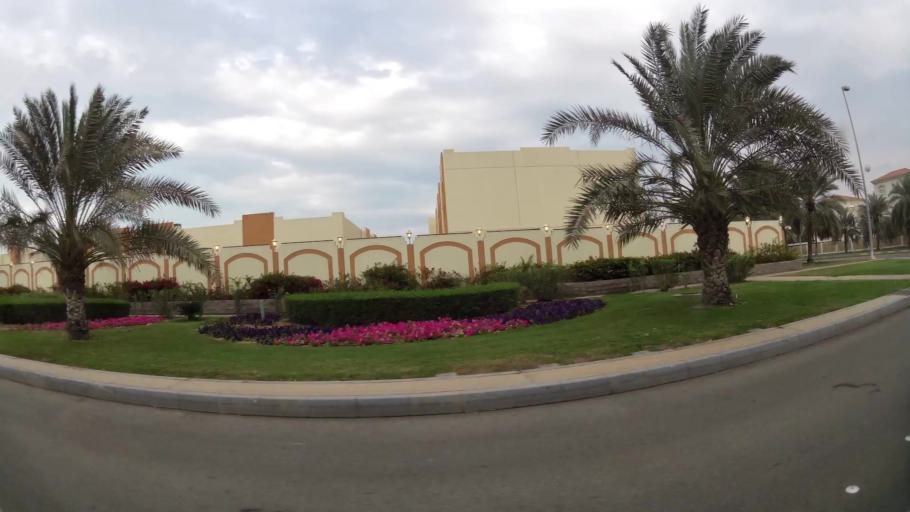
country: AE
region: Abu Dhabi
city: Abu Dhabi
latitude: 24.4465
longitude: 54.3560
